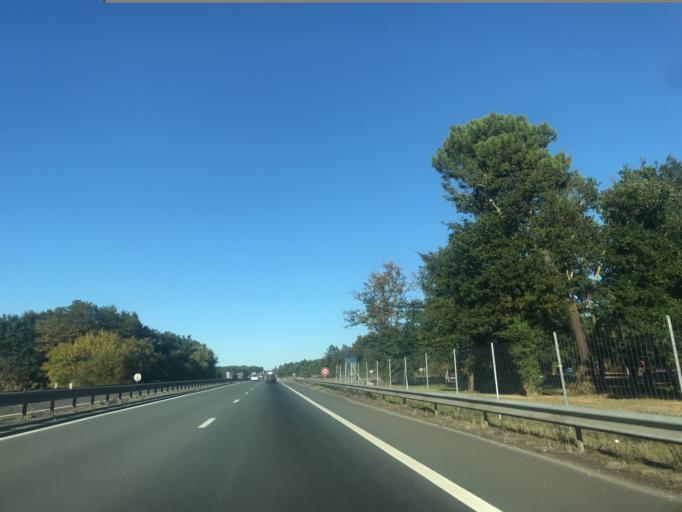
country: FR
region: Aquitaine
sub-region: Departement de la Gironde
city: Laruscade
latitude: 45.1706
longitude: -0.3347
